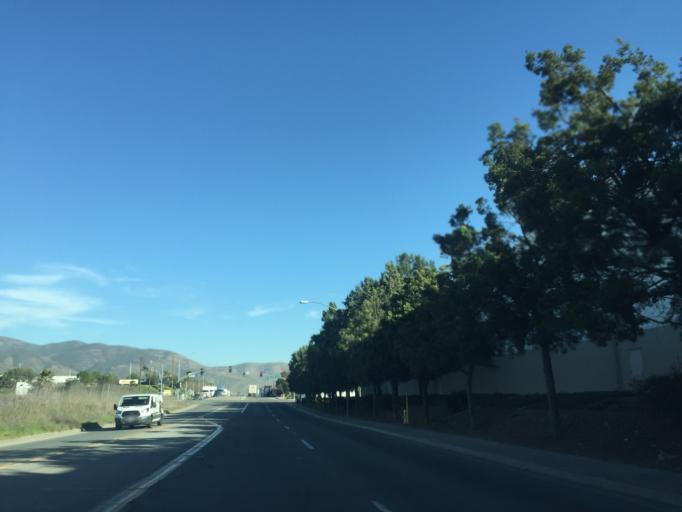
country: MX
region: Baja California
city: Tijuana
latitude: 32.5601
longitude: -116.9295
